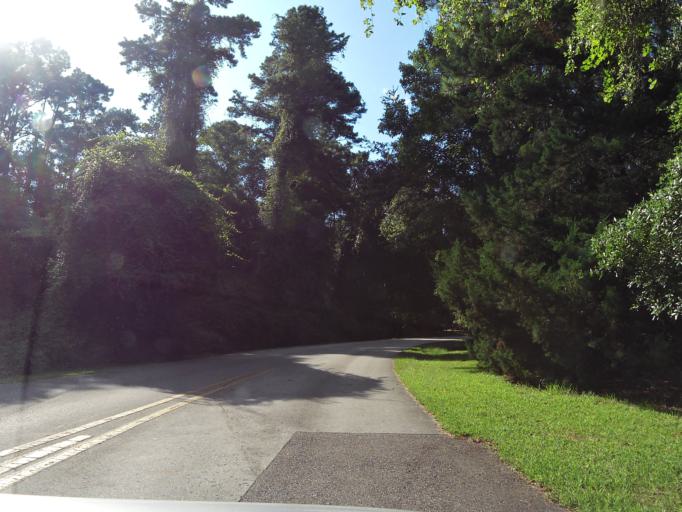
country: US
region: Florida
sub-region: Clay County
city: Orange Park
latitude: 30.2269
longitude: -81.7022
